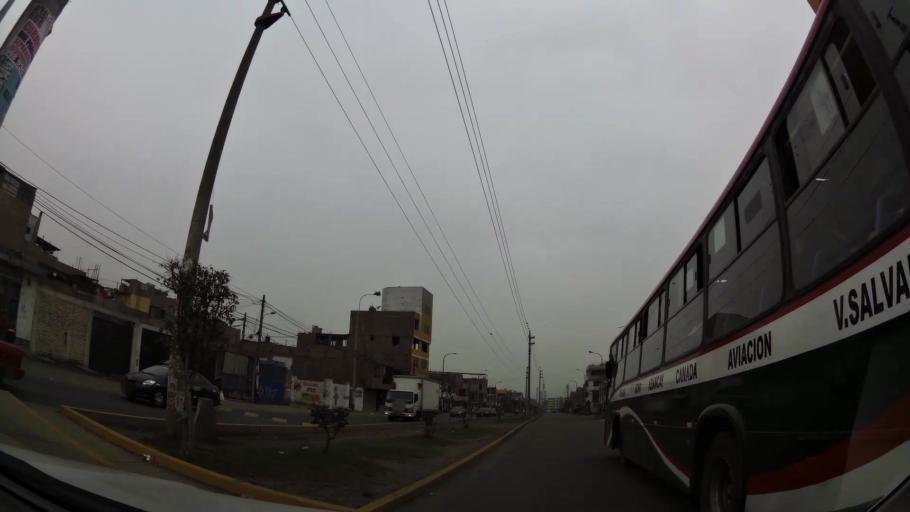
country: PE
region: Lima
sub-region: Lima
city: Independencia
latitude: -11.9505
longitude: -76.9809
